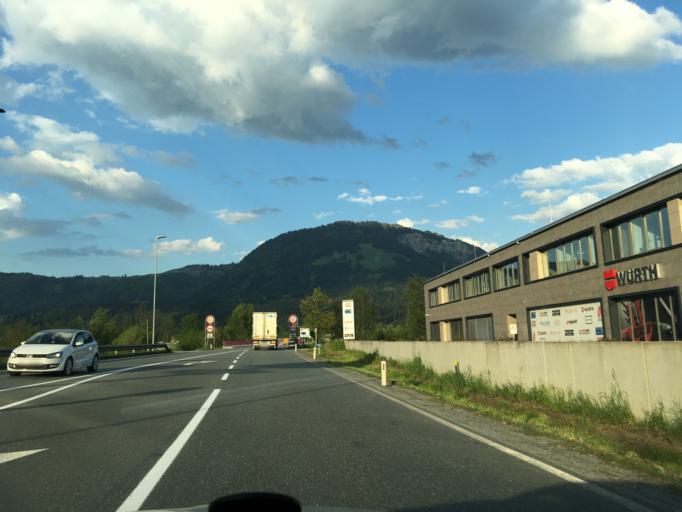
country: AT
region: Tyrol
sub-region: Politischer Bezirk Kitzbuhel
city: Sankt Johann in Tirol
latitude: 47.5291
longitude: 12.4274
